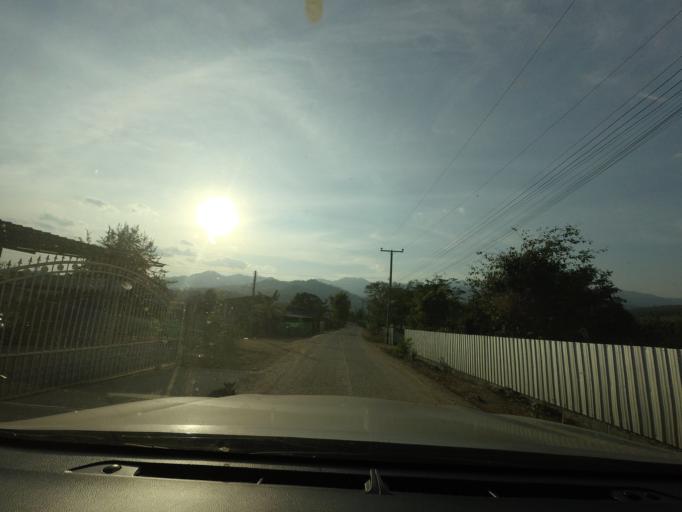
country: TH
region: Mae Hong Son
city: Mae Hi
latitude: 19.3407
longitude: 98.4274
